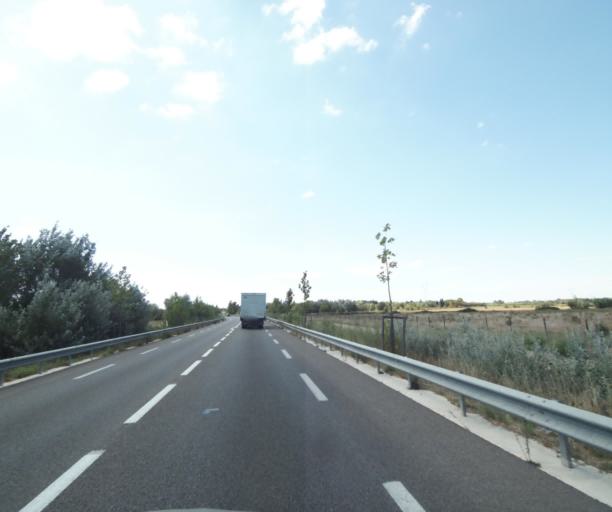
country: FR
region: Languedoc-Roussillon
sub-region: Departement du Gard
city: Rodilhan
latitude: 43.8147
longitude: 4.4132
